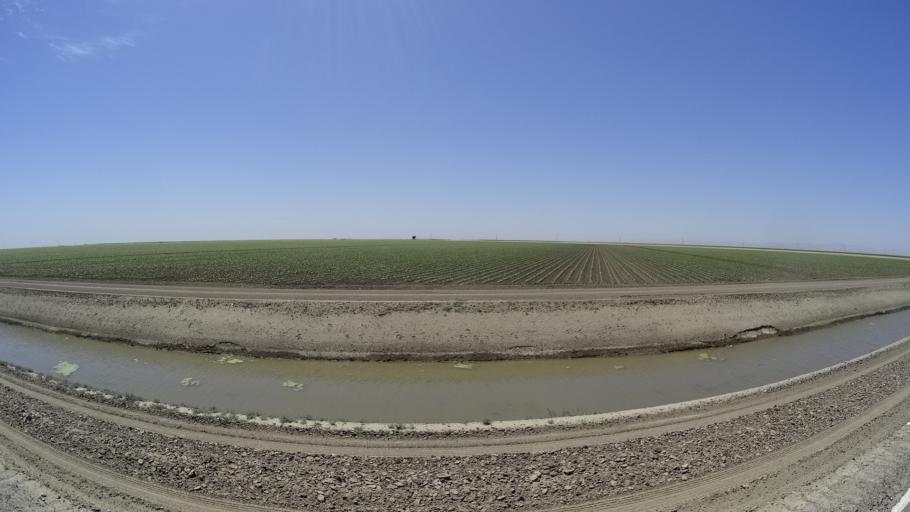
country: US
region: California
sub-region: Kings County
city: Corcoran
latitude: 36.1162
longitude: -119.6771
